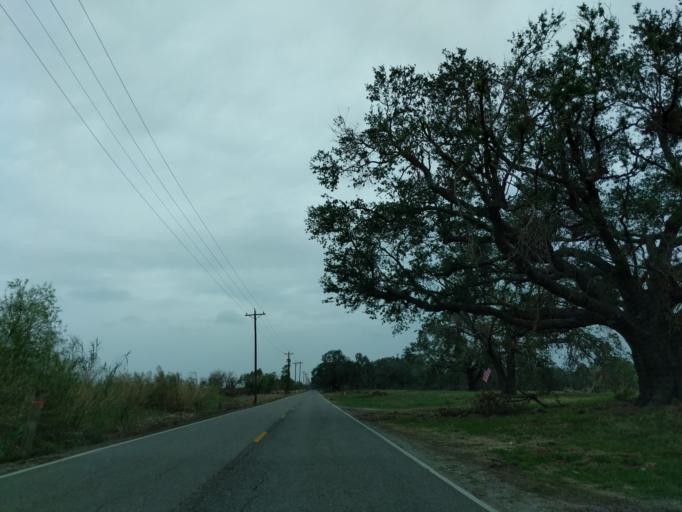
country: US
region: Louisiana
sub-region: Jefferson Davis Parish
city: Lake Arthur
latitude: 29.7537
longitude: -92.9157
